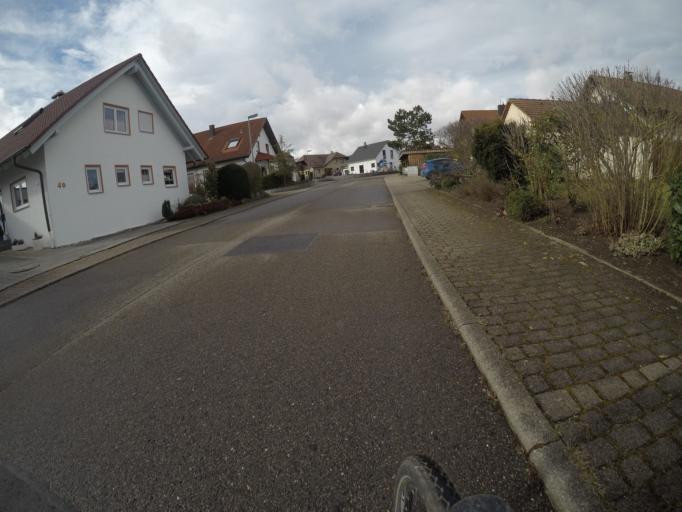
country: DE
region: Baden-Wuerttemberg
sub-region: Regierungsbezirk Stuttgart
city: Herrenberg
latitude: 48.6062
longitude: 8.8457
